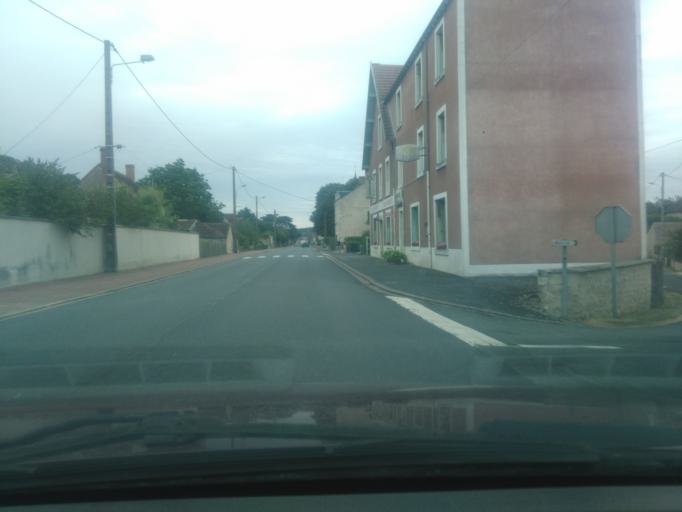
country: FR
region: Centre
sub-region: Departement de l'Indre
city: Saint-Gaultier
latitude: 46.6362
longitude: 1.3577
